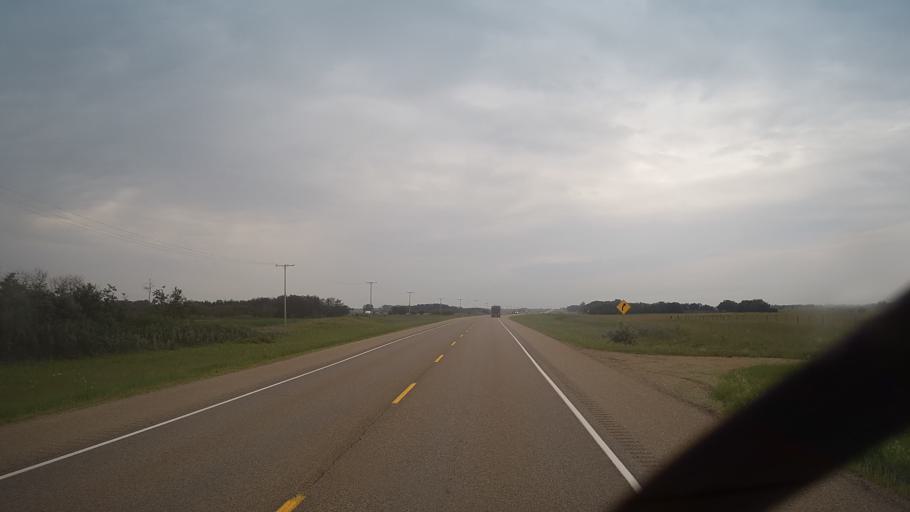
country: CA
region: Saskatchewan
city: Langham
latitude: 52.1291
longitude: -107.1101
